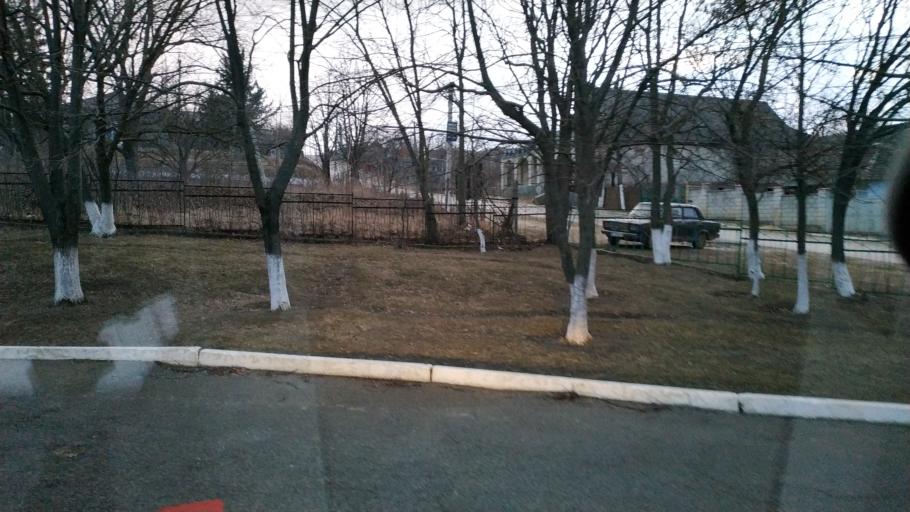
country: MD
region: Calarasi
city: Calarasi
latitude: 47.3744
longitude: 28.3208
